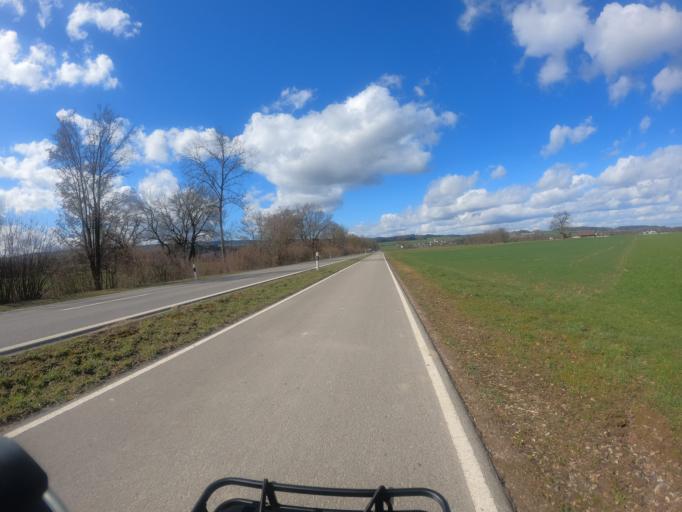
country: CH
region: Zurich
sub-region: Bezirk Affoltern
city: Ottenbach
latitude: 47.2797
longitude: 8.3880
